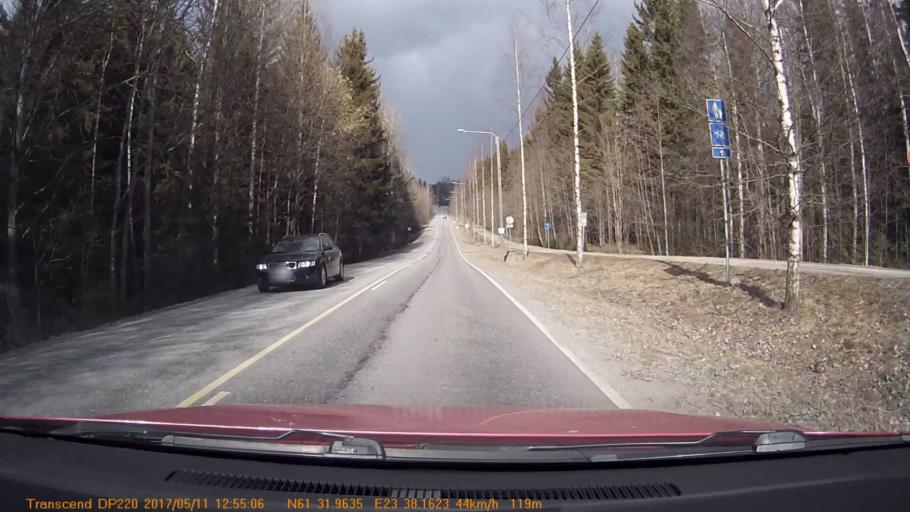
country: FI
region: Pirkanmaa
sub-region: Tampere
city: Yloejaervi
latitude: 61.5327
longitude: 23.6360
